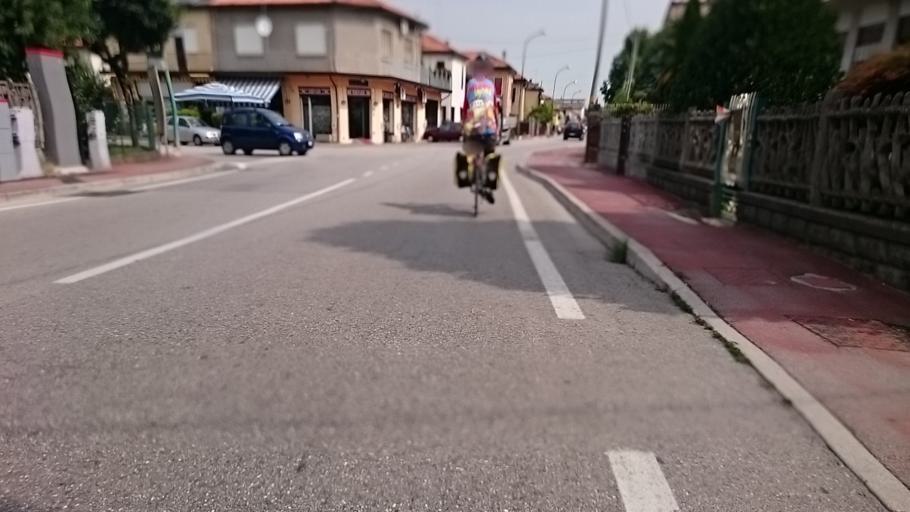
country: IT
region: Veneto
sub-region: Provincia di Venezia
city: Fornase
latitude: 45.4570
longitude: 12.1738
